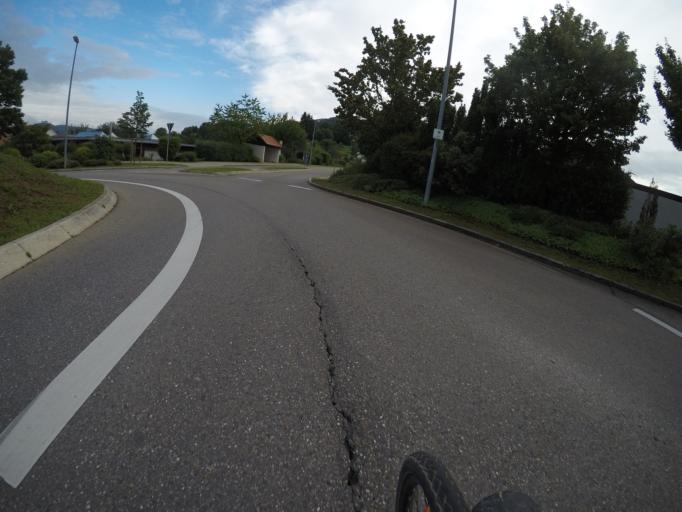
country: DE
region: Baden-Wuerttemberg
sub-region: Regierungsbezirk Stuttgart
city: Kohlberg
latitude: 48.5619
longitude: 9.3309
